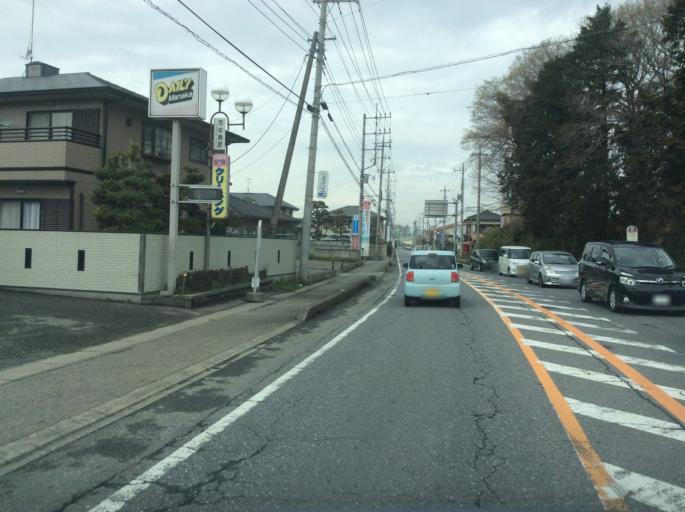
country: JP
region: Ibaraki
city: Iwai
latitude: 36.0045
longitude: 139.9057
